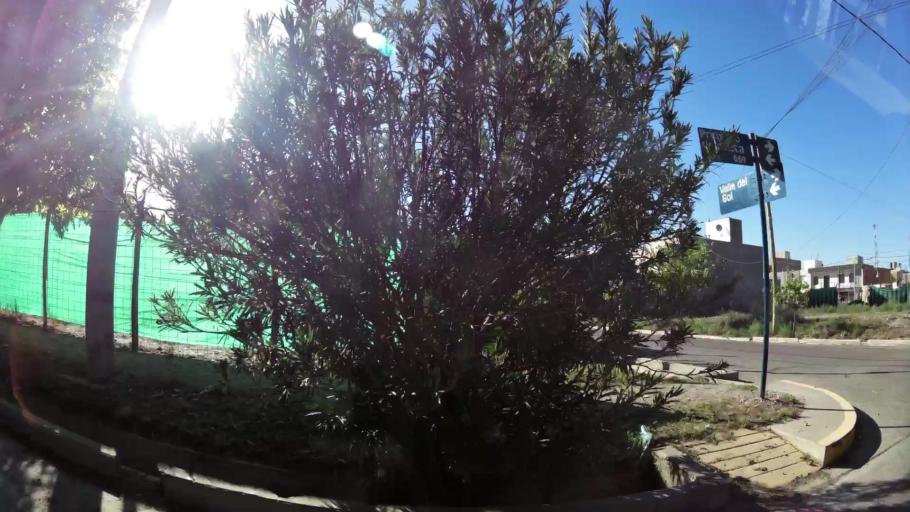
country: AR
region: Mendoza
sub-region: Departamento de Godoy Cruz
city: Godoy Cruz
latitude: -32.9334
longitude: -68.8312
